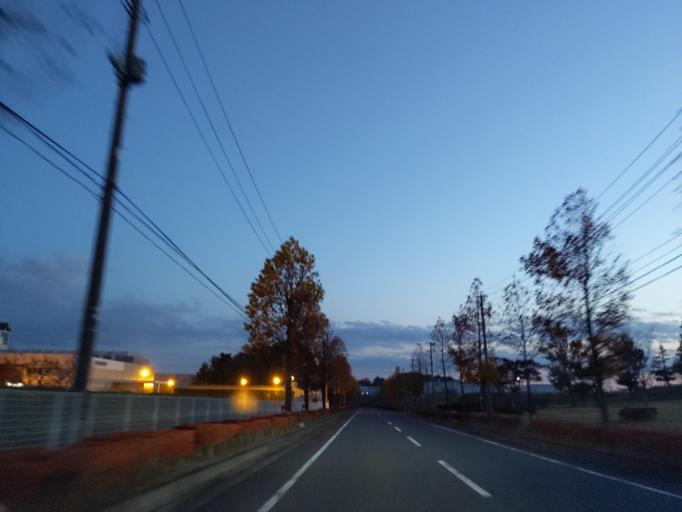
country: JP
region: Fukushima
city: Koriyama
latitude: 37.4469
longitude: 140.3056
